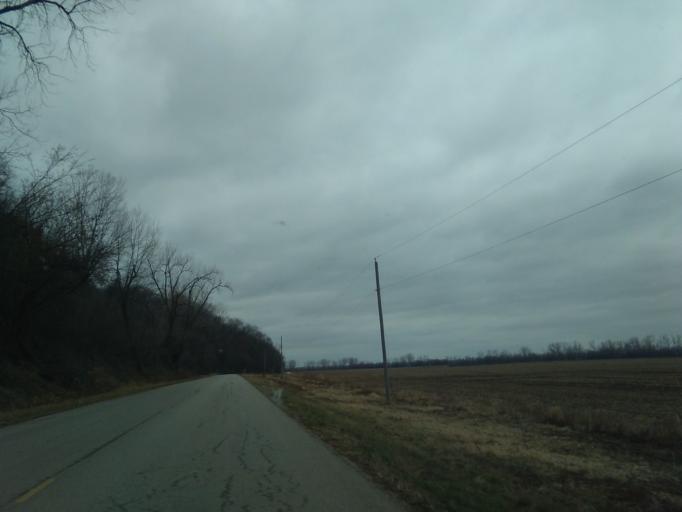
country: US
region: Missouri
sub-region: Holt County
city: Mound City
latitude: 40.0244
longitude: -95.3560
